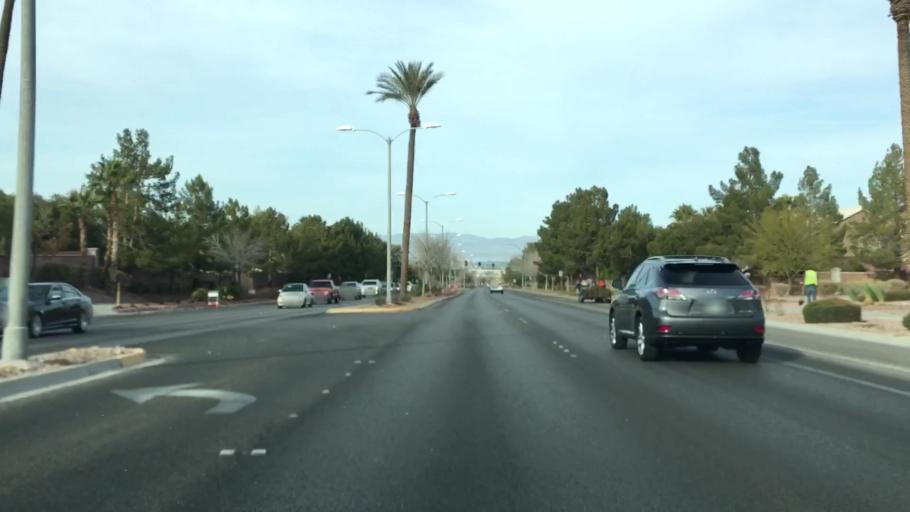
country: US
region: Nevada
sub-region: Clark County
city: Whitney
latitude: 36.0126
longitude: -115.0830
